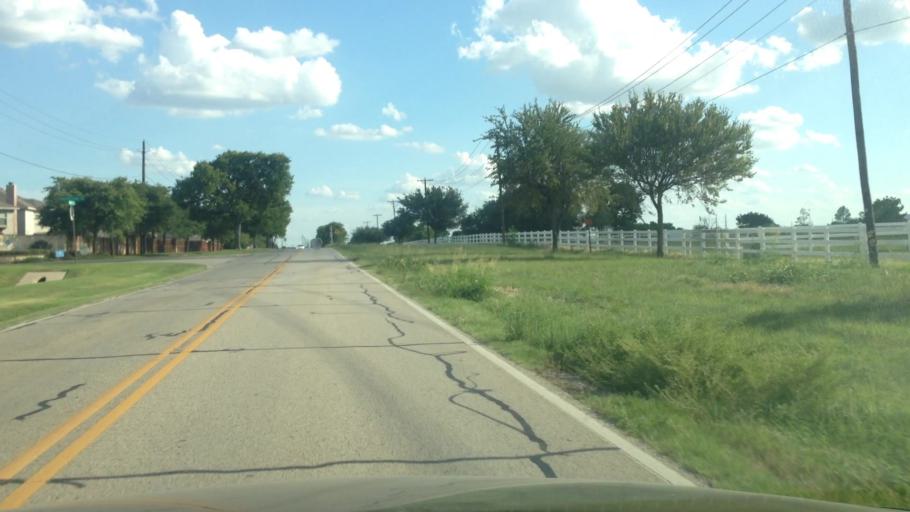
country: US
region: Texas
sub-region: Tarrant County
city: Haslet
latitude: 32.9206
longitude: -97.3749
